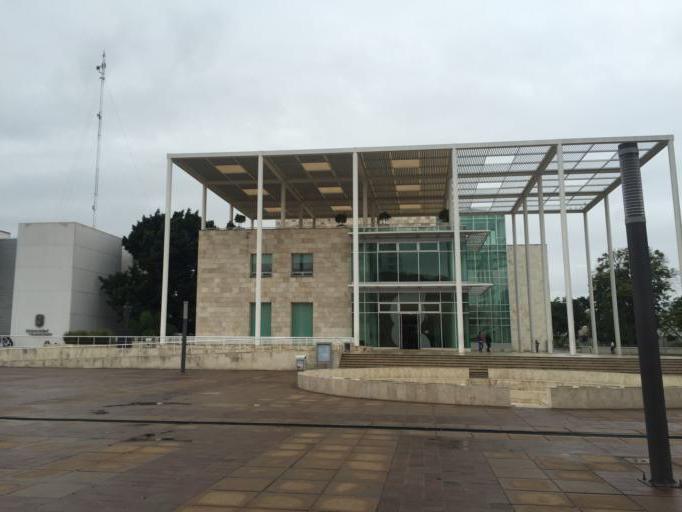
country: MX
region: Guanajuato
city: Leon
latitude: 21.1166
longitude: -101.6603
